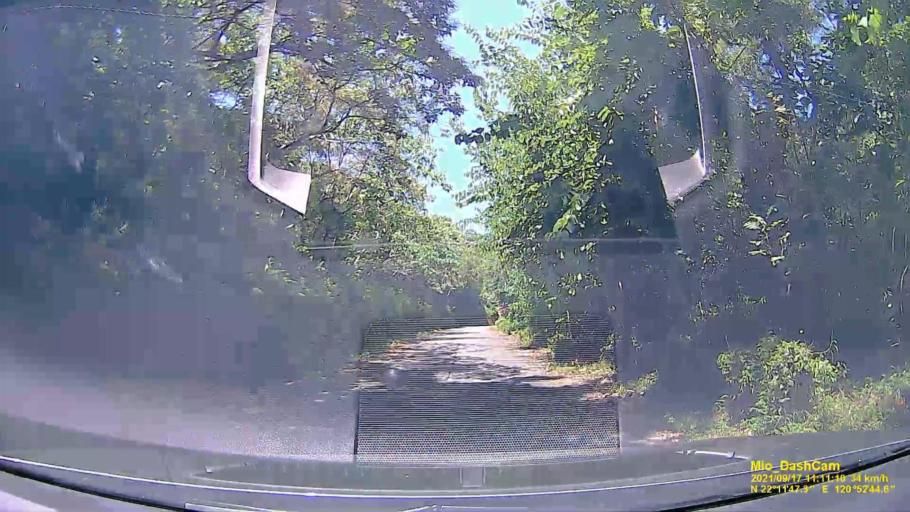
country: TW
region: Taiwan
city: Hengchun
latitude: 22.1965
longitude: 120.8790
